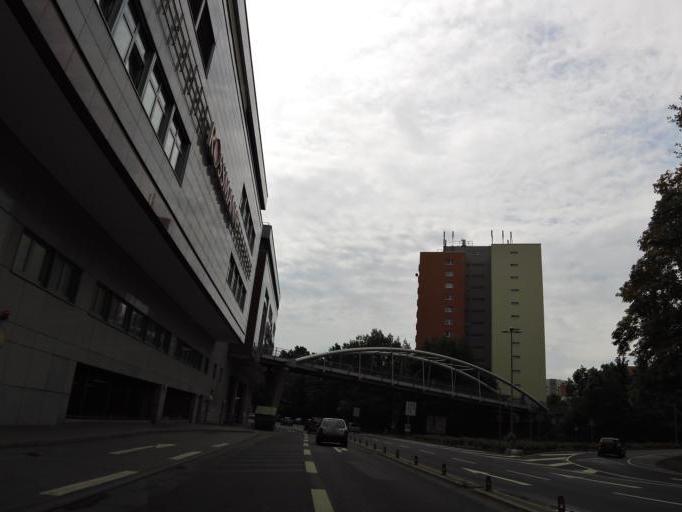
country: DE
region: Hesse
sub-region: Regierungsbezirk Darmstadt
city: Steinbach am Taunus
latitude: 50.1566
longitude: 8.6316
